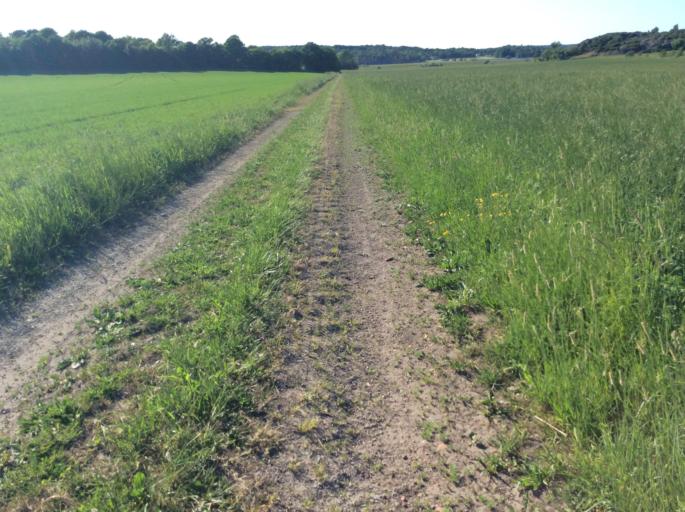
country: SE
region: Vaestra Goetaland
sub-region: Goteborg
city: Majorna
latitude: 57.7971
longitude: 11.8766
